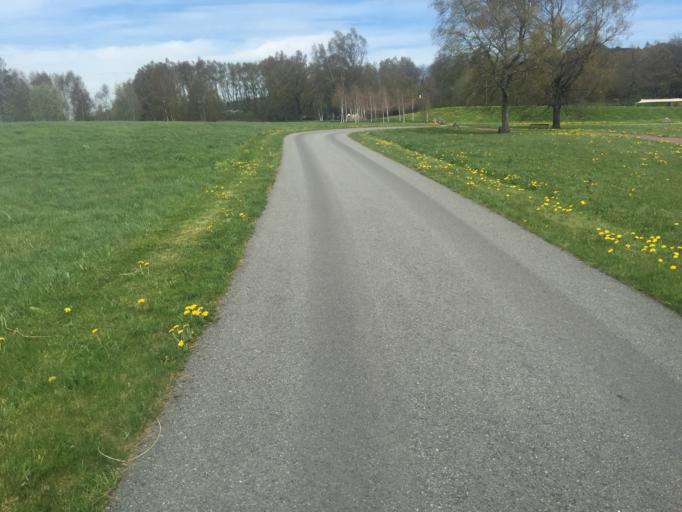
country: FR
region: Auvergne
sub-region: Departement du Puy-de-Dome
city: Saint-Ours
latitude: 45.8136
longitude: 2.9381
